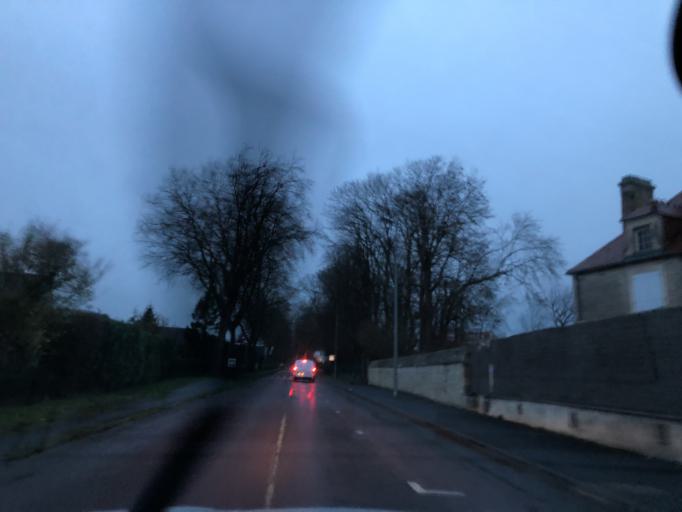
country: FR
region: Lower Normandy
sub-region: Departement du Calvados
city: Mathieu
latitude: 49.2571
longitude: -0.3738
